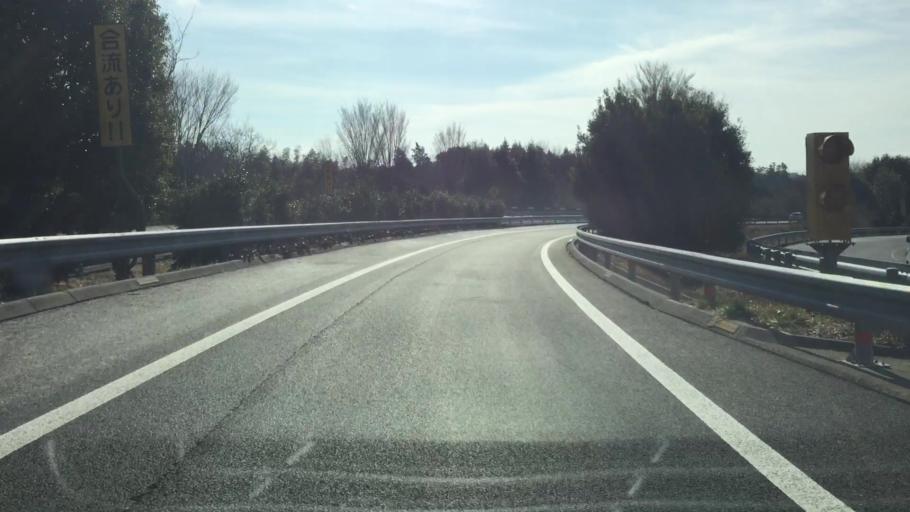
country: JP
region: Ibaraki
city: Tomobe
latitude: 36.3217
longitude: 140.3484
